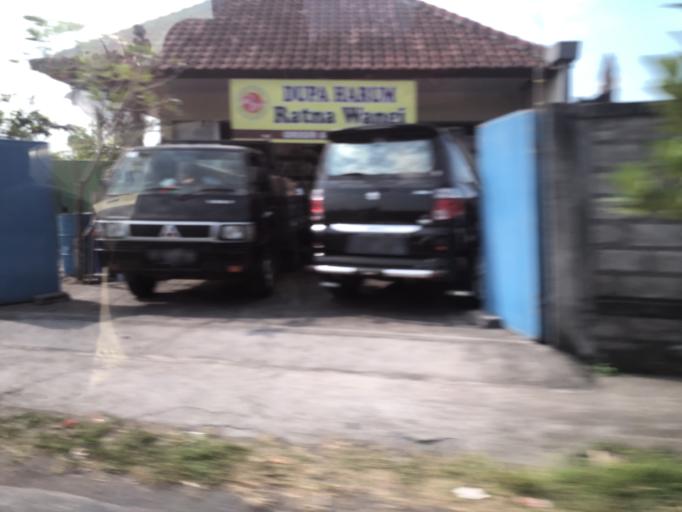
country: ID
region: Bali
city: Banjar Bucu
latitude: -8.5771
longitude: 115.1999
